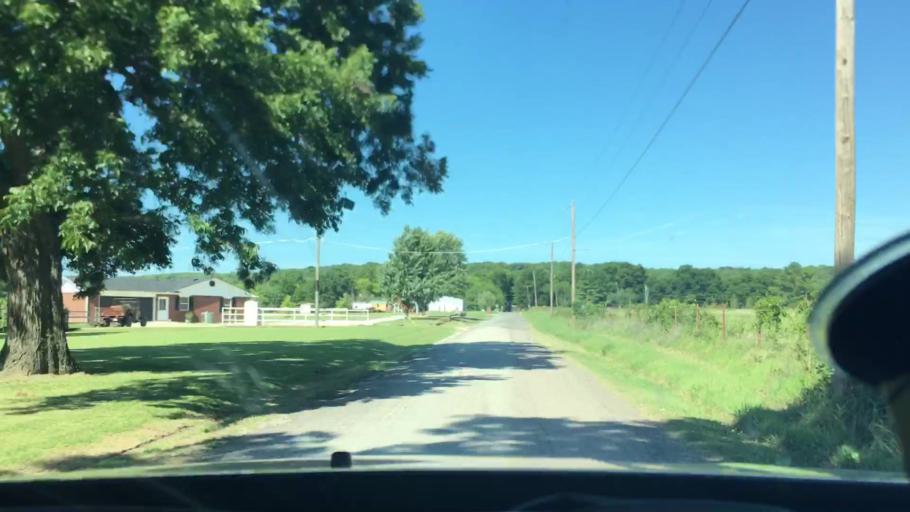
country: US
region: Oklahoma
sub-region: Pontotoc County
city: Ada
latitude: 34.7237
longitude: -96.6664
